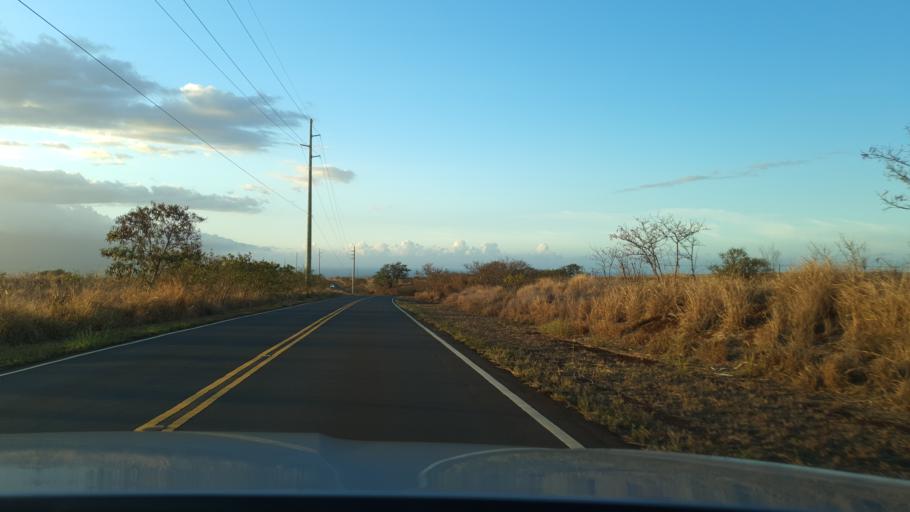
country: US
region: Hawaii
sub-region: Maui County
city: Pukalani
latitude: 20.8114
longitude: -156.3825
